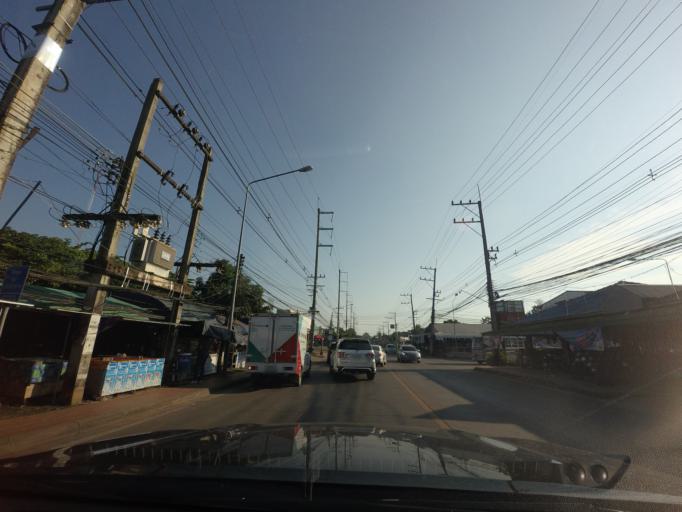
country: TH
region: Nan
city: Nan
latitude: 18.7730
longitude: 100.7655
